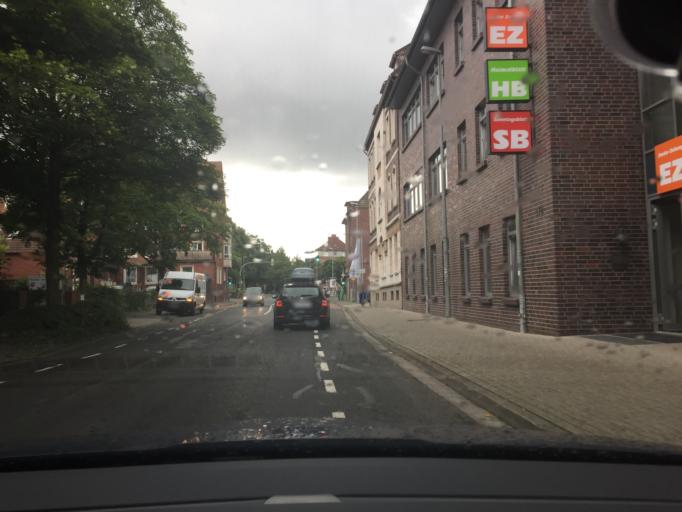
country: DE
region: Lower Saxony
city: Emden
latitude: 53.3676
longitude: 7.1995
